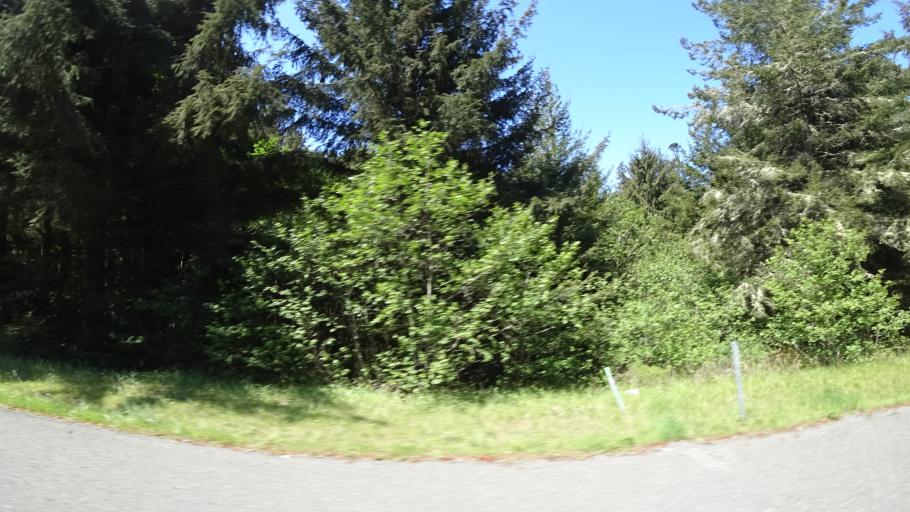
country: US
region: California
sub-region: Humboldt County
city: Westhaven-Moonstone
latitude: 41.1059
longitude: -124.1549
